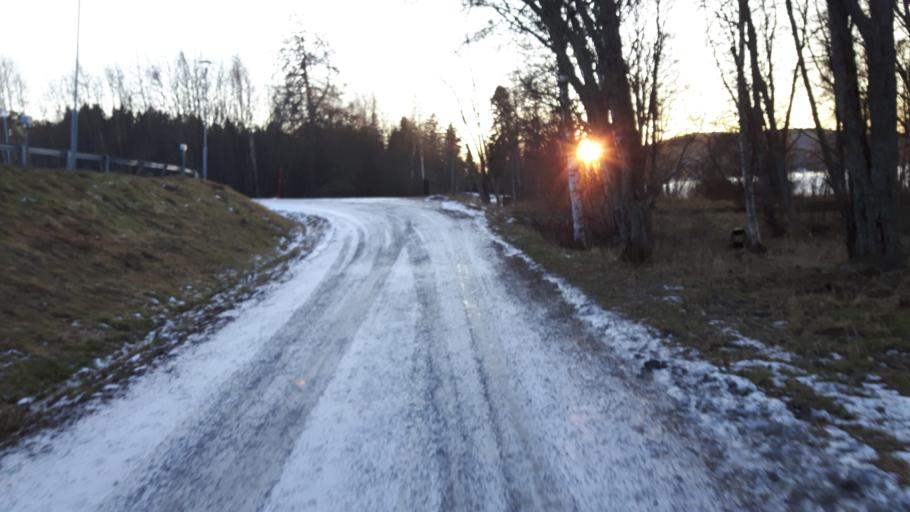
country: SE
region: Vaesternorrland
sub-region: Haernoesands Kommun
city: Haernoesand
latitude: 62.6209
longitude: 17.9360
